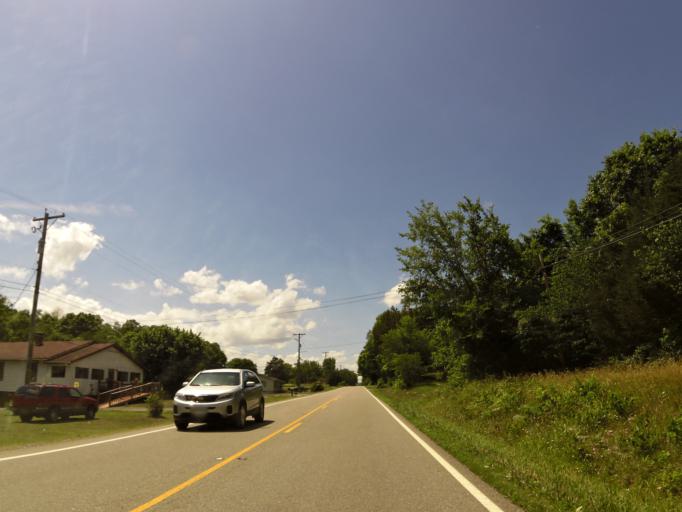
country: US
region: Virginia
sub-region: Lee County
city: Dryden
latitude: 36.7119
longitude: -82.9678
